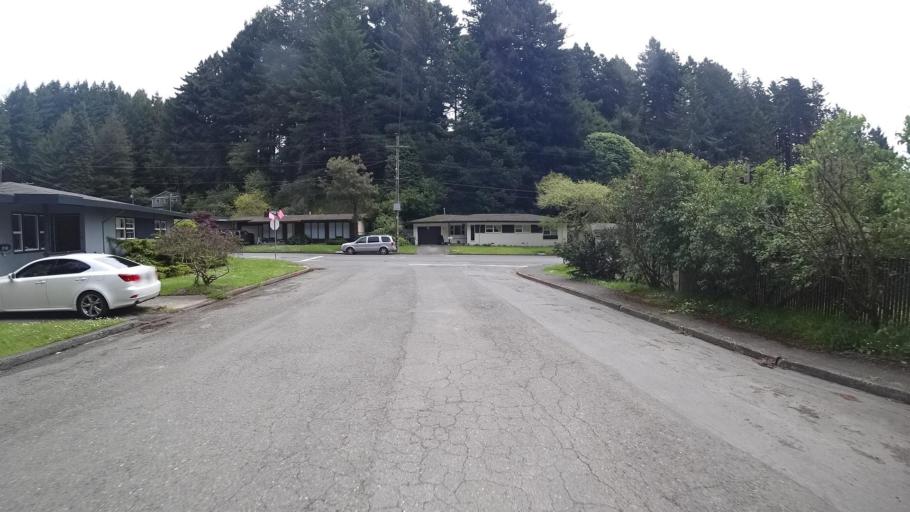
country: US
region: California
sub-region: Humboldt County
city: Arcata
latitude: 40.8614
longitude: -124.0678
